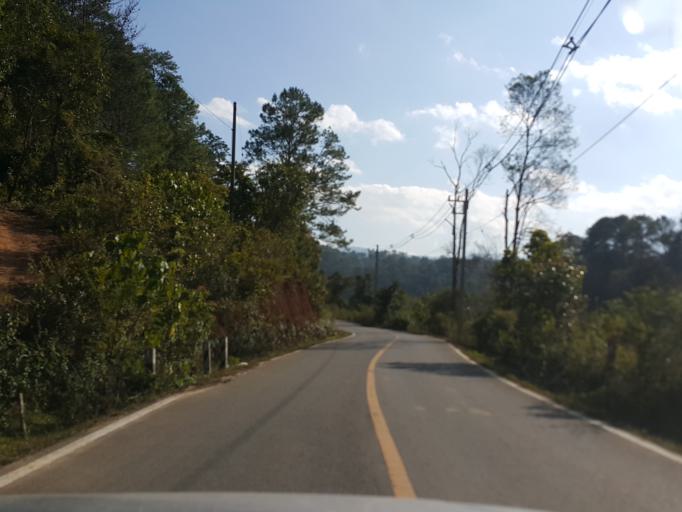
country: TH
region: Chiang Mai
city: Mae Wang
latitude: 18.6644
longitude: 98.5500
